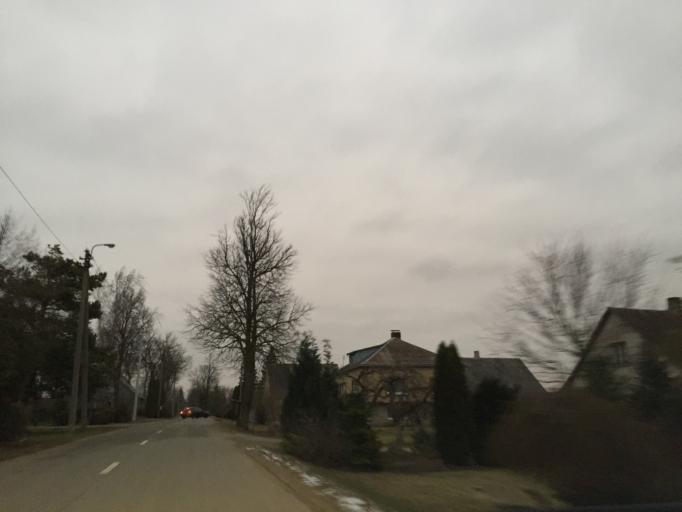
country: LT
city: Zagare
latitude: 56.3380
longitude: 23.2953
